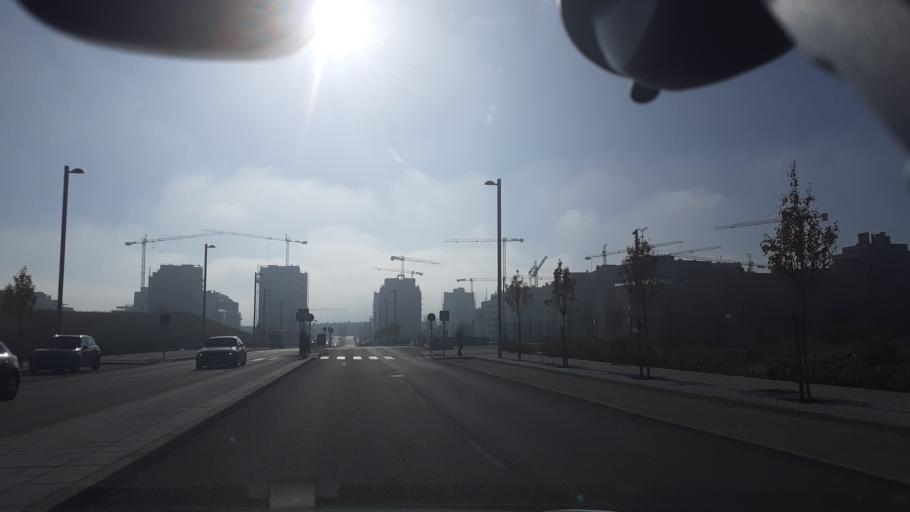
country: ES
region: Madrid
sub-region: Provincia de Madrid
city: Coslada
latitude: 40.4034
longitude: -3.5549
